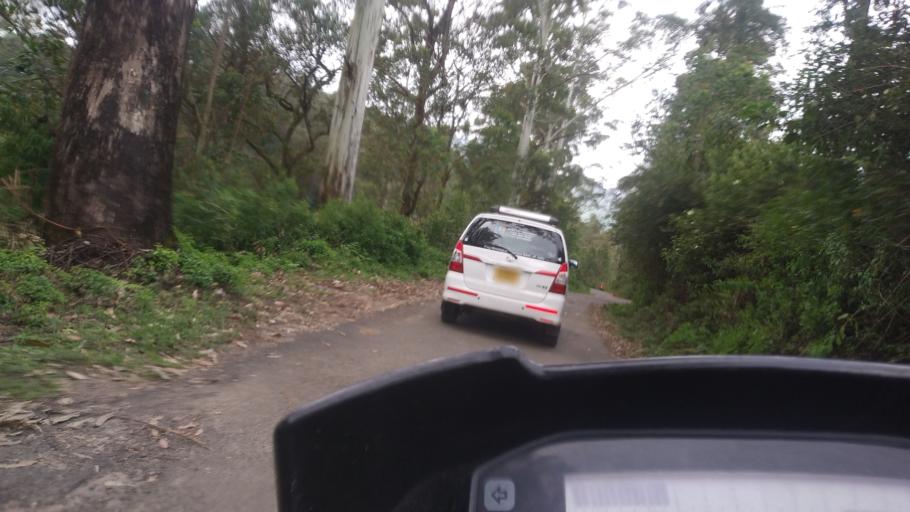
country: IN
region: Kerala
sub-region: Idukki
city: Munnar
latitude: 10.0611
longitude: 77.1069
